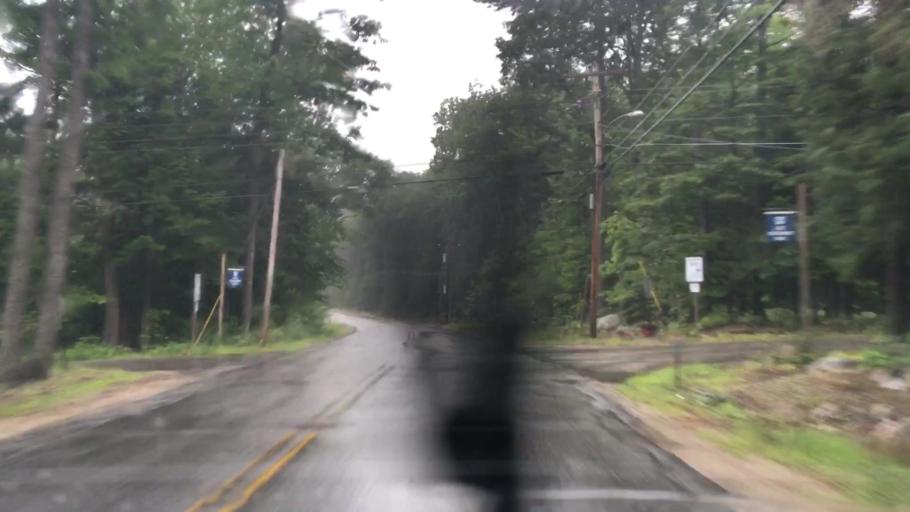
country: US
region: Maine
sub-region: Oxford County
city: Lovell
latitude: 44.0721
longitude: -70.8212
